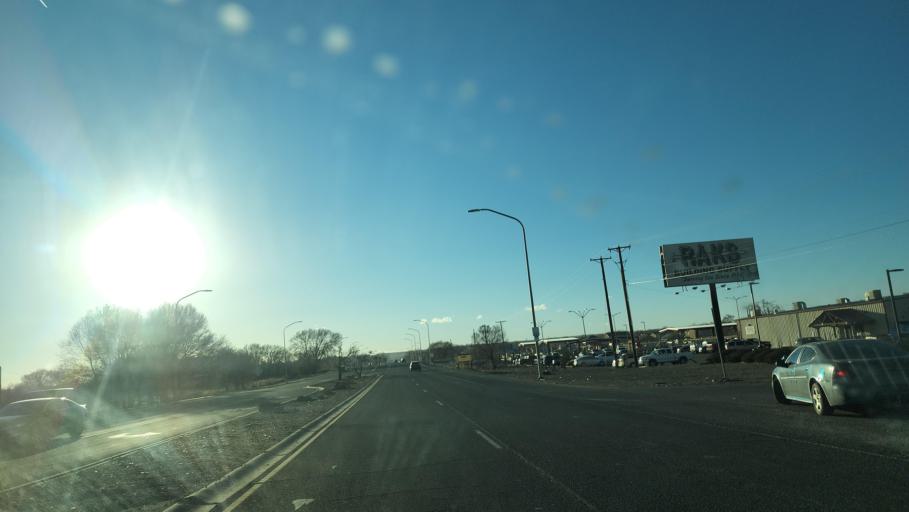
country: US
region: New Mexico
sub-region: Bernalillo County
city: South Valley
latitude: 35.0272
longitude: -106.6586
